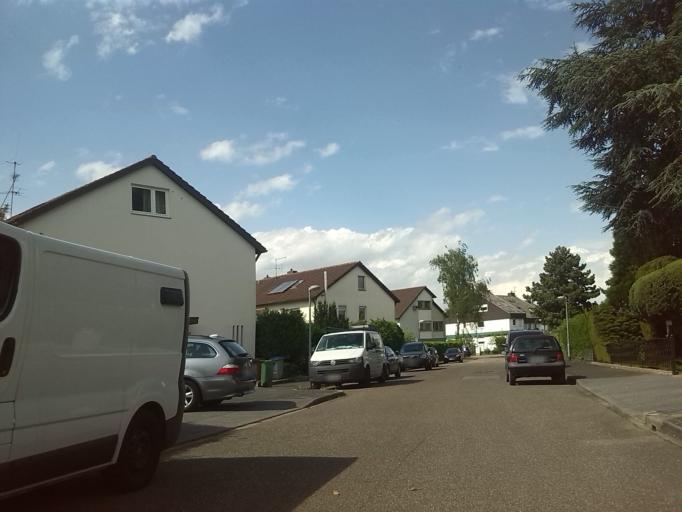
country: DE
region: Baden-Wuerttemberg
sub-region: Karlsruhe Region
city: Ilvesheim
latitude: 49.4592
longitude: 8.5704
